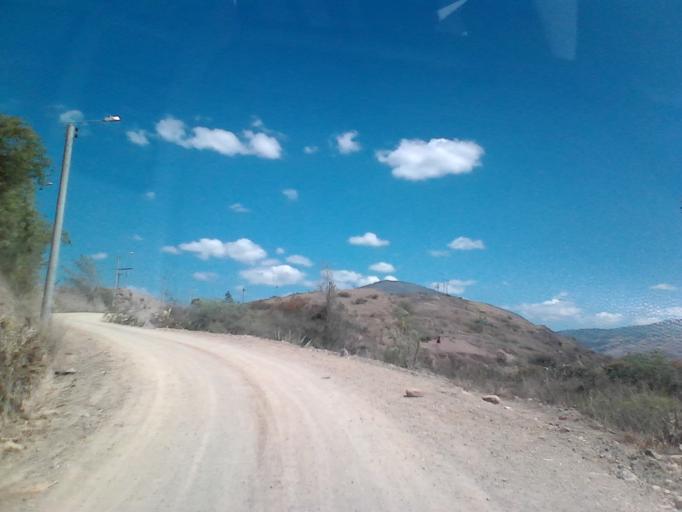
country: CO
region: Boyaca
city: Sachica
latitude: 5.5756
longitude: -73.5477
